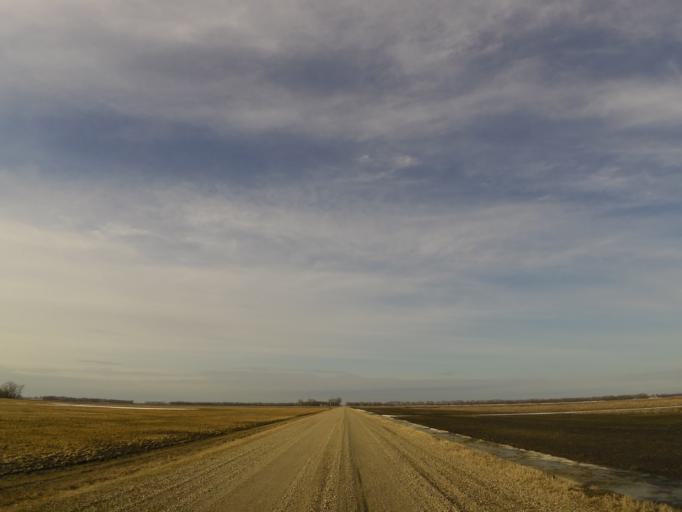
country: US
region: North Dakota
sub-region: Walsh County
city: Grafton
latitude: 48.4224
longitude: -97.2123
